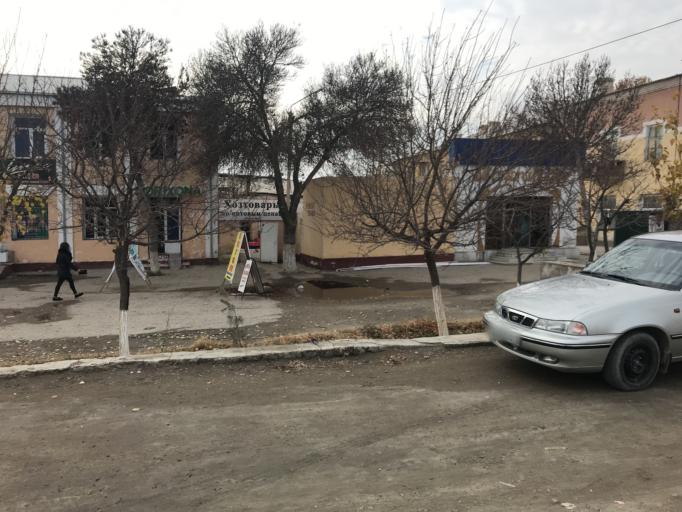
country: UZ
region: Bukhara
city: Kogon
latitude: 39.7264
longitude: 64.5423
